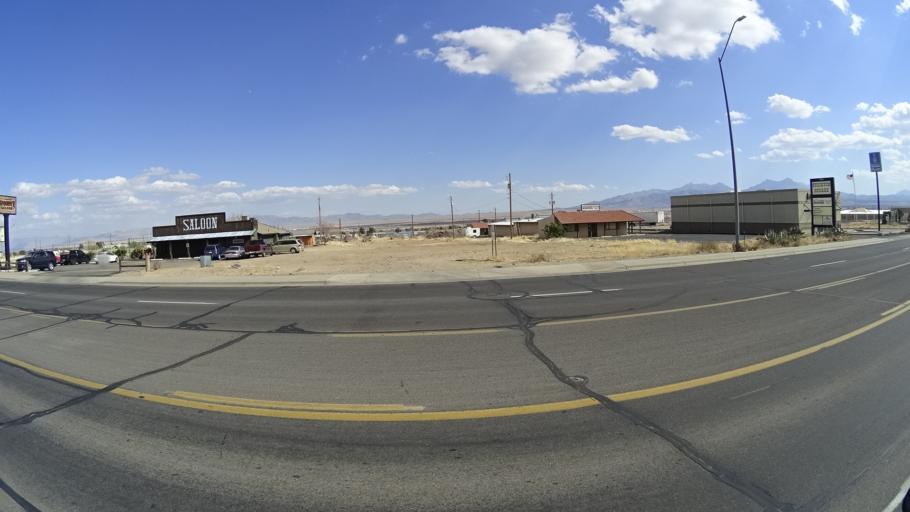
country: US
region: Arizona
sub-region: Mohave County
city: New Kingman-Butler
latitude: 35.2511
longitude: -114.0390
